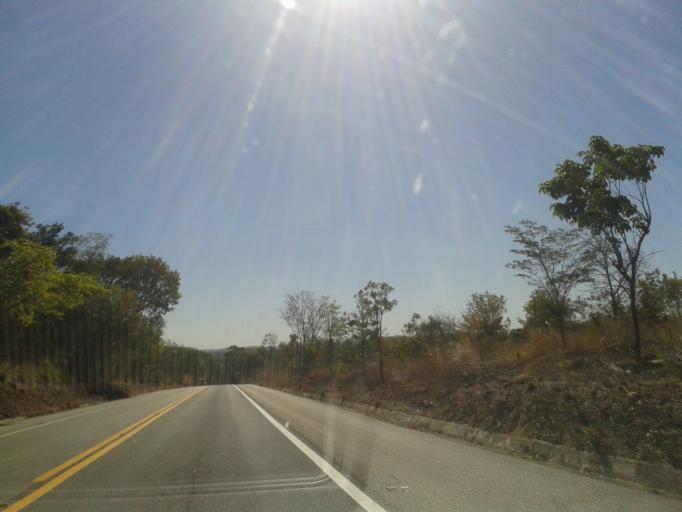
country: BR
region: Goias
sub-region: Goias
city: Goias
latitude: -15.7724
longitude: -50.1453
